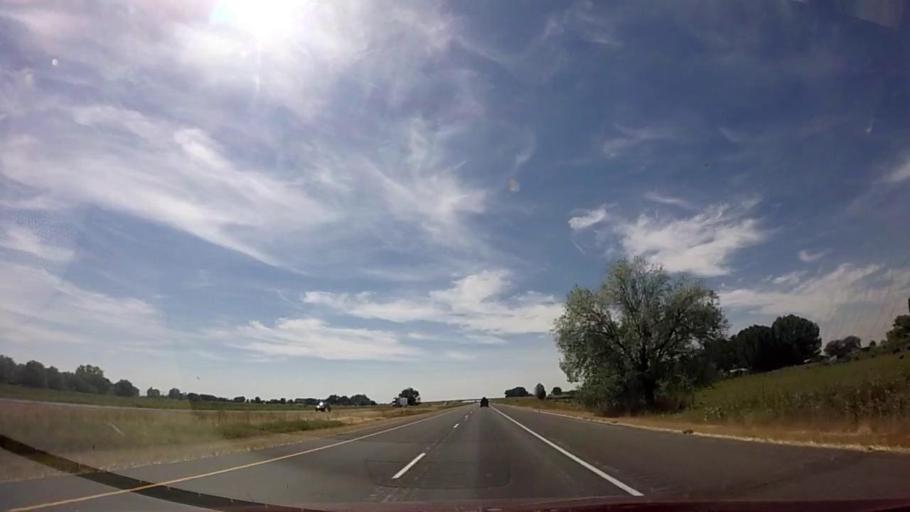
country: US
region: Idaho
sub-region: Minidoka County
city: Rupert
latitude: 42.5690
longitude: -113.6948
